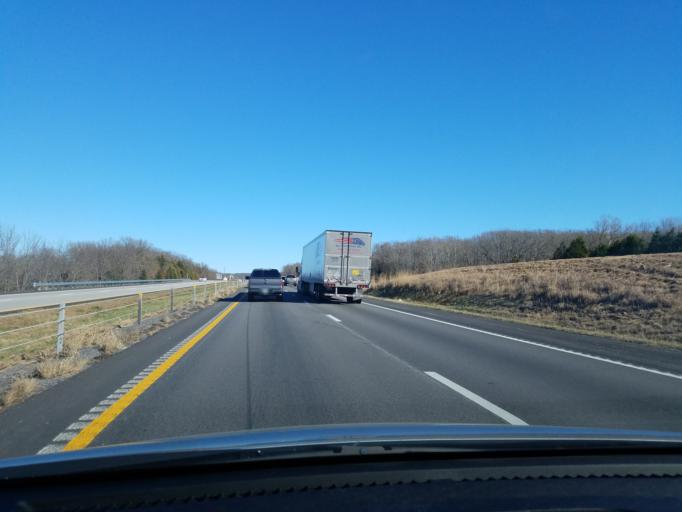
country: US
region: Missouri
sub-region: Webster County
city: Marshfield
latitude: 37.3043
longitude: -92.9817
